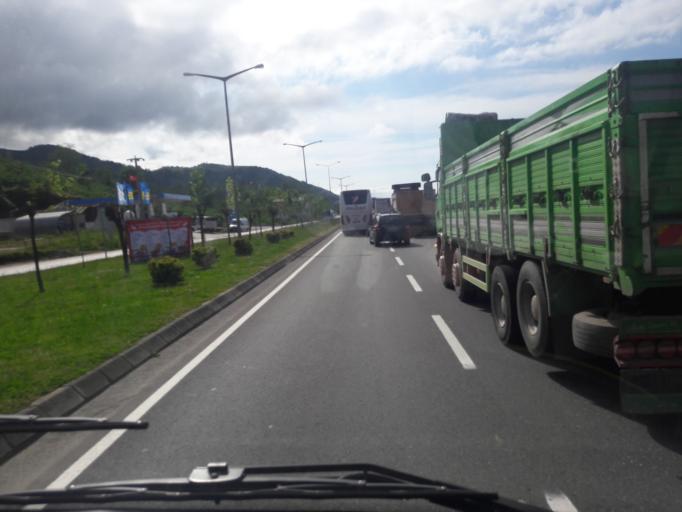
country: TR
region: Ordu
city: Gulyali
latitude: 40.9649
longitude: 38.0734
